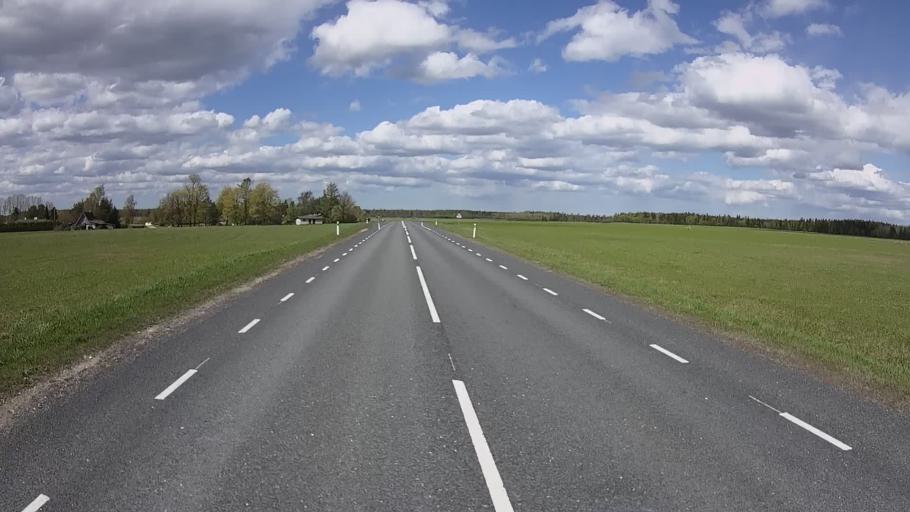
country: EE
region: Jaervamaa
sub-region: Jaerva-Jaani vald
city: Jarva-Jaani
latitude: 59.1138
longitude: 25.7947
